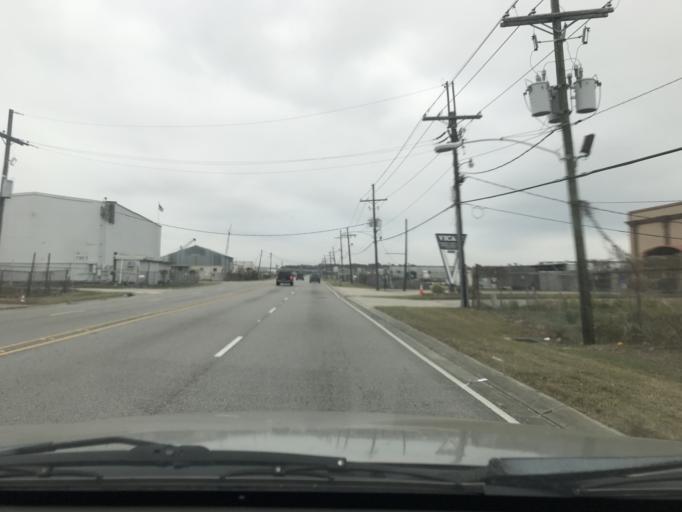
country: US
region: Louisiana
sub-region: Jefferson Parish
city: Woodmere
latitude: 29.8786
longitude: -90.0748
